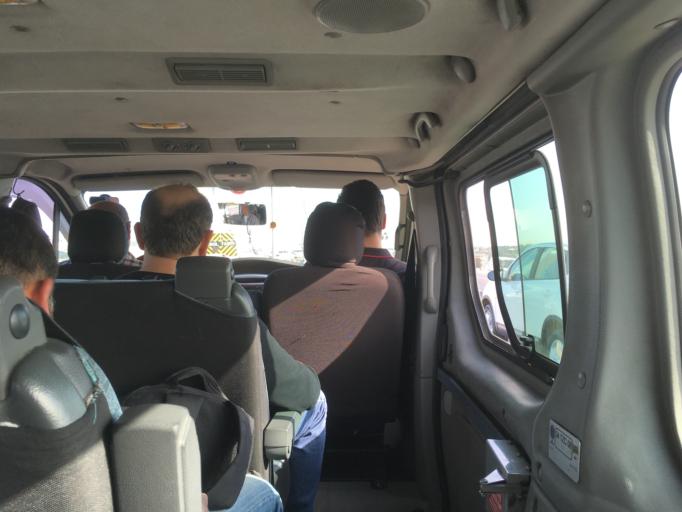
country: TR
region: Istanbul
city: UEskuedar
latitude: 41.0499
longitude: 29.0297
